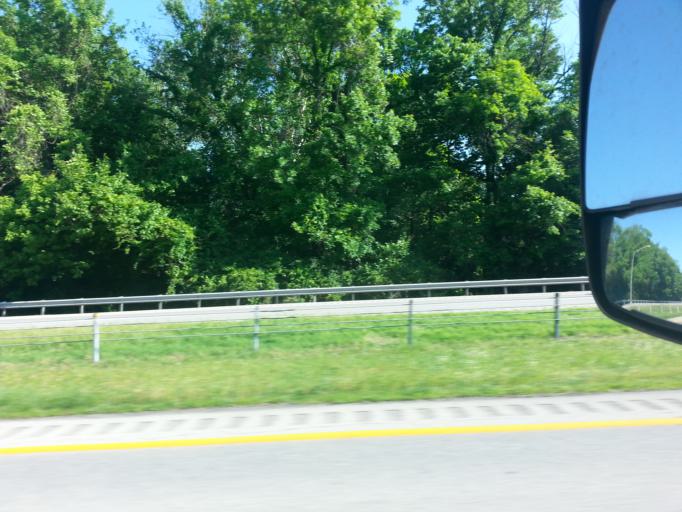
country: US
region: Kentucky
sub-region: Jefferson County
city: Saint Matthews
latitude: 38.2352
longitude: -85.6521
